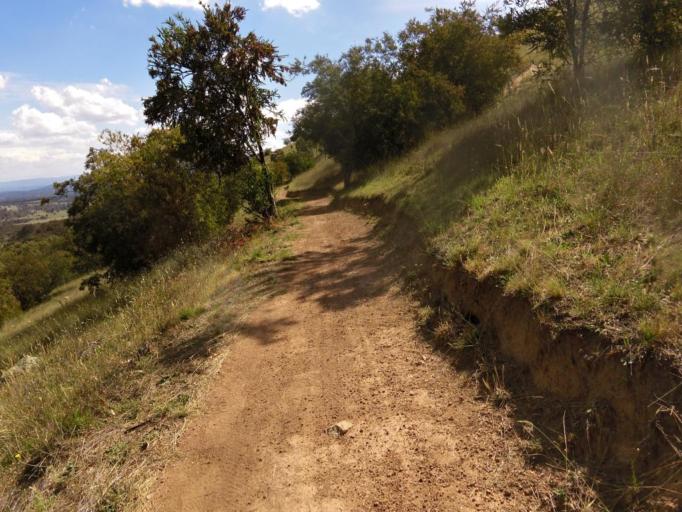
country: AU
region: Australian Capital Territory
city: Belconnen
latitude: -35.1484
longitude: 149.0898
